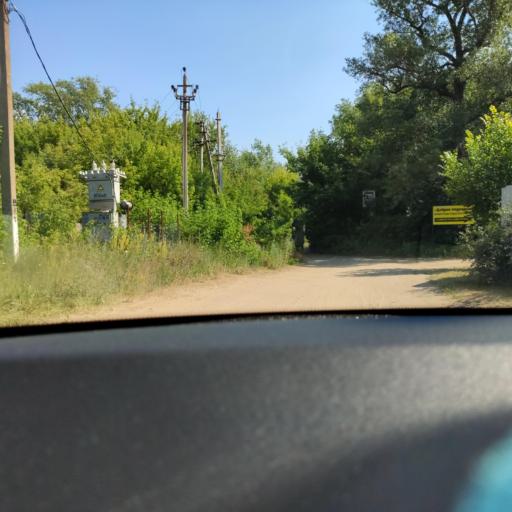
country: RU
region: Samara
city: Volzhskiy
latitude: 53.4370
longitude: 50.1662
